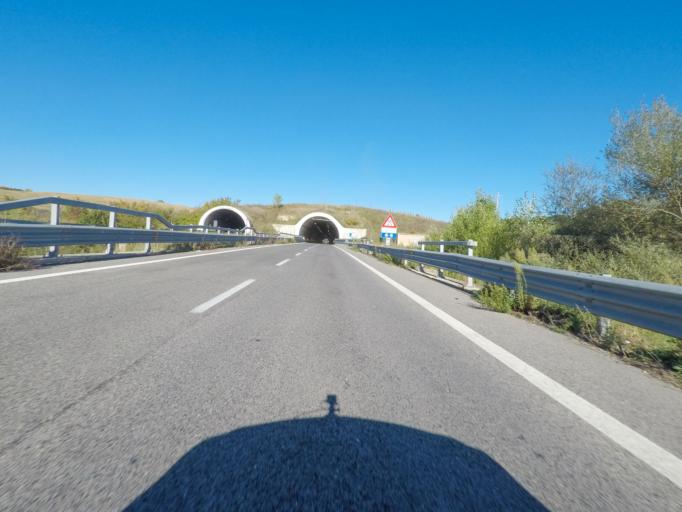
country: IT
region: Tuscany
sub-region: Provincia di Siena
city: Rosia
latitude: 43.2458
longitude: 11.2900
